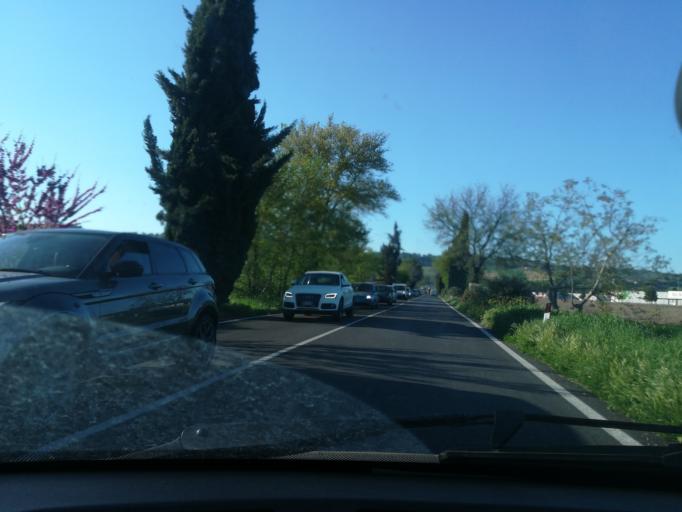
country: IT
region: The Marches
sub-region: Provincia di Macerata
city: Piediripa
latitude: 43.2768
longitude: 13.4858
